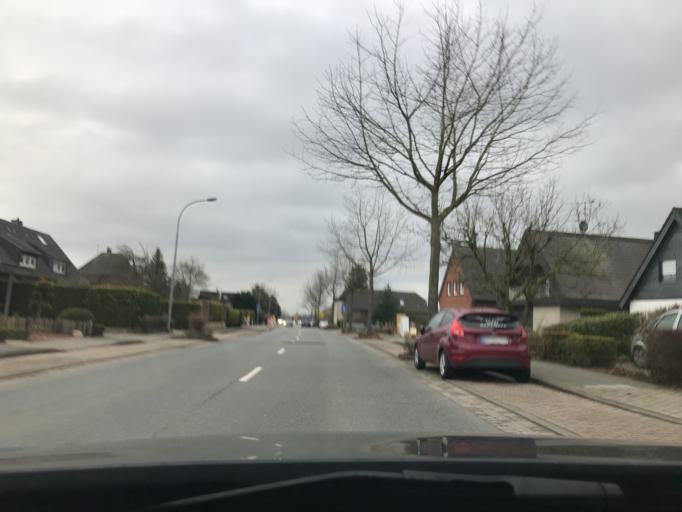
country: DE
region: North Rhine-Westphalia
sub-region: Regierungsbezirk Dusseldorf
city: Uedem
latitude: 51.6632
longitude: 6.2755
